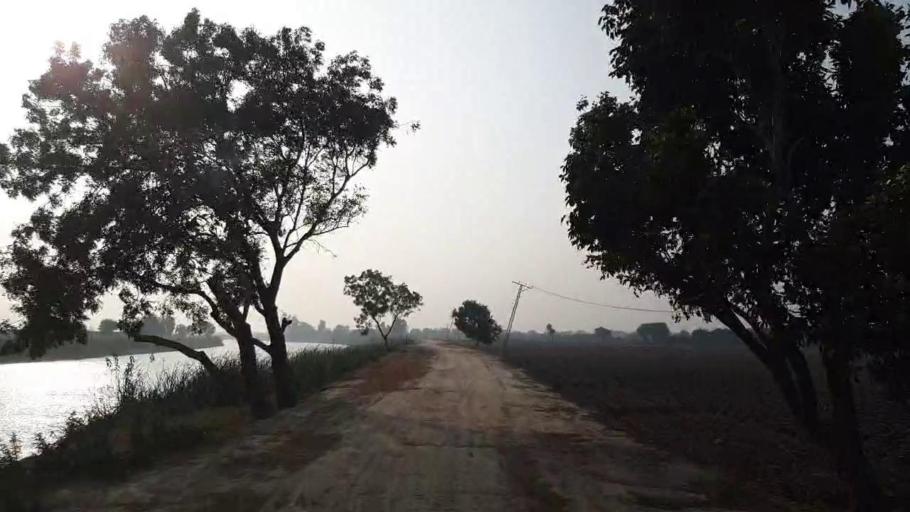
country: PK
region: Sindh
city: Tando Muhammad Khan
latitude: 25.0951
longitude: 68.5775
